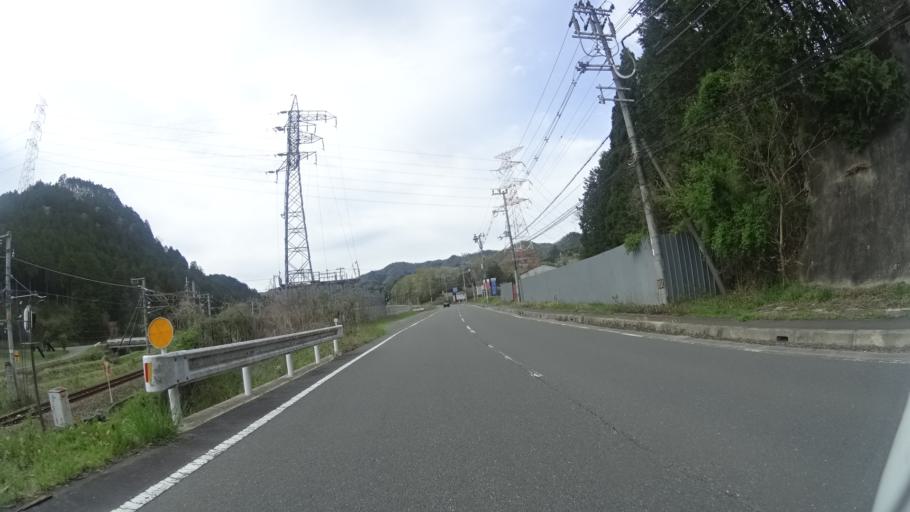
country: JP
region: Kyoto
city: Kameoka
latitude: 35.1847
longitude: 135.4851
